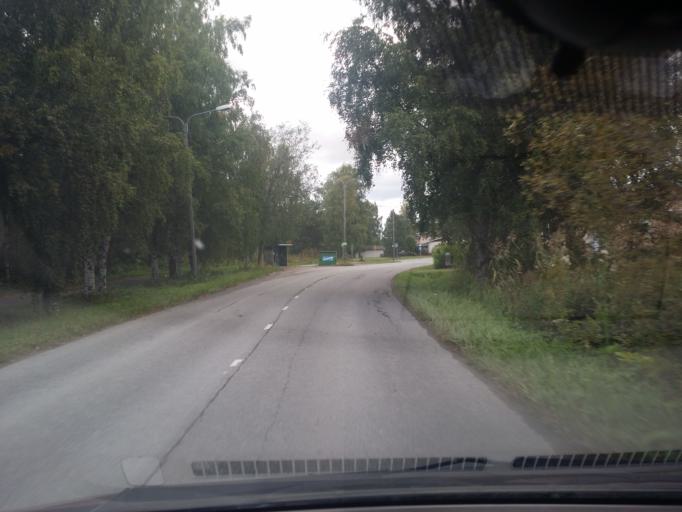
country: FI
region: Satakunta
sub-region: Pori
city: Pori
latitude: 61.5026
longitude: 21.8033
